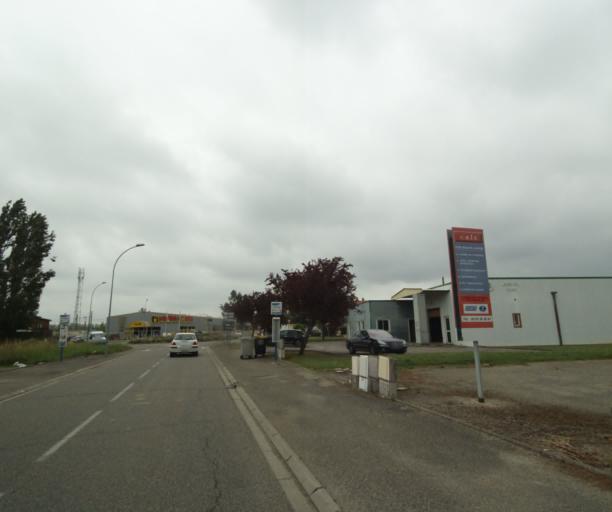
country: FR
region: Midi-Pyrenees
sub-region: Departement du Tarn-et-Garonne
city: Montauban
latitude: 43.9954
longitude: 1.3344
